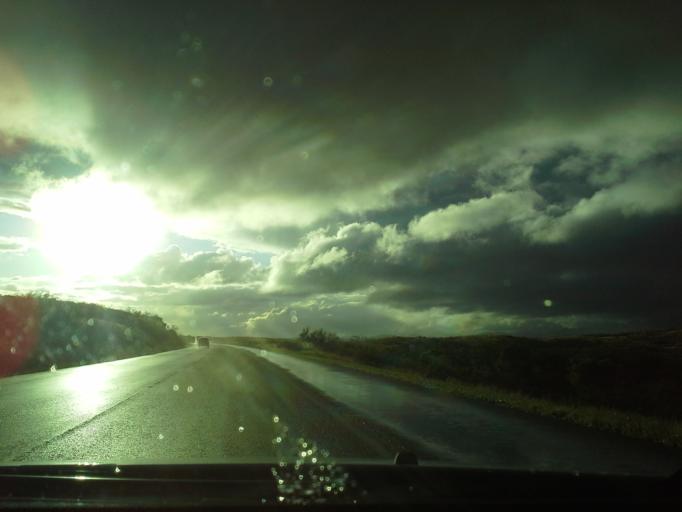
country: US
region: Arizona
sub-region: Cochise County
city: Mescal
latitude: 31.9712
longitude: -110.4777
